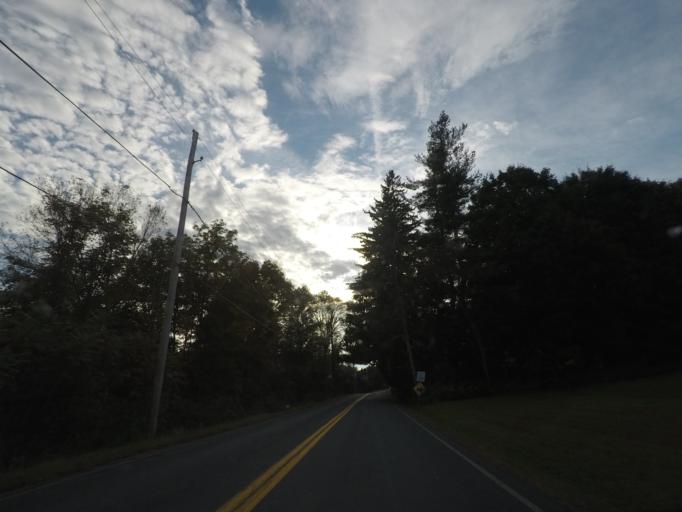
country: US
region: New York
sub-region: Rensselaer County
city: West Sand Lake
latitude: 42.6329
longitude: -73.6281
